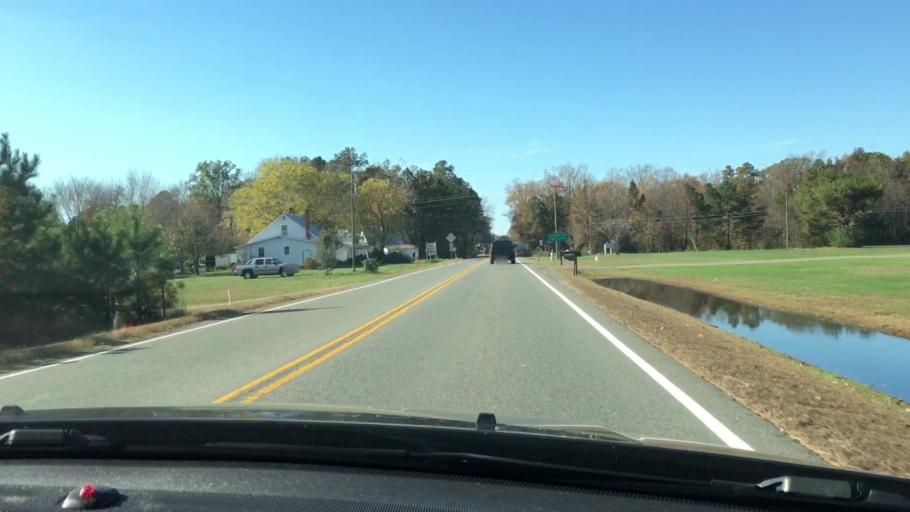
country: US
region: Virginia
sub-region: Hanover County
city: Hanover
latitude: 37.8328
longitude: -77.3641
